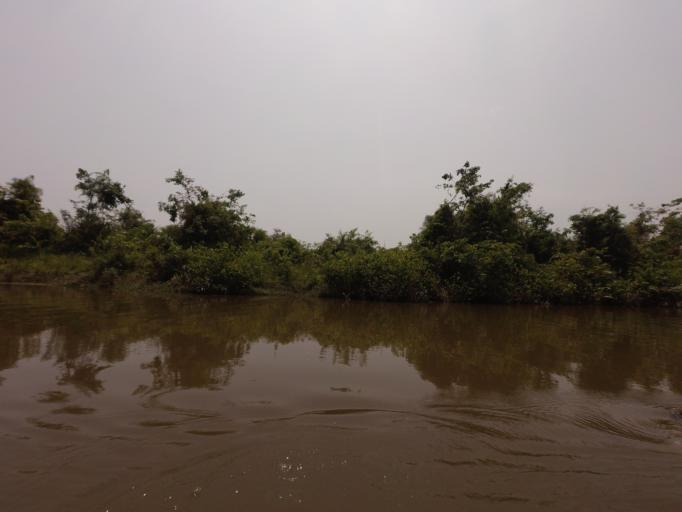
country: BD
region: Sylhet
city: Sylhet
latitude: 25.0125
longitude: 91.9160
